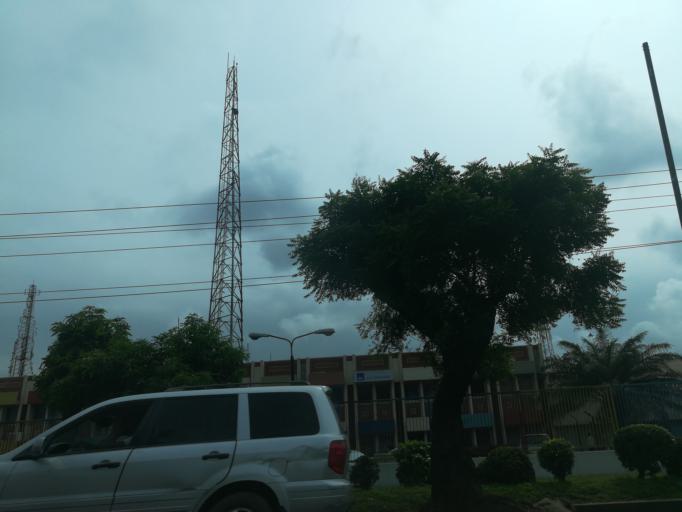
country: NG
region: Lagos
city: Ojota
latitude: 6.6049
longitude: 3.3714
